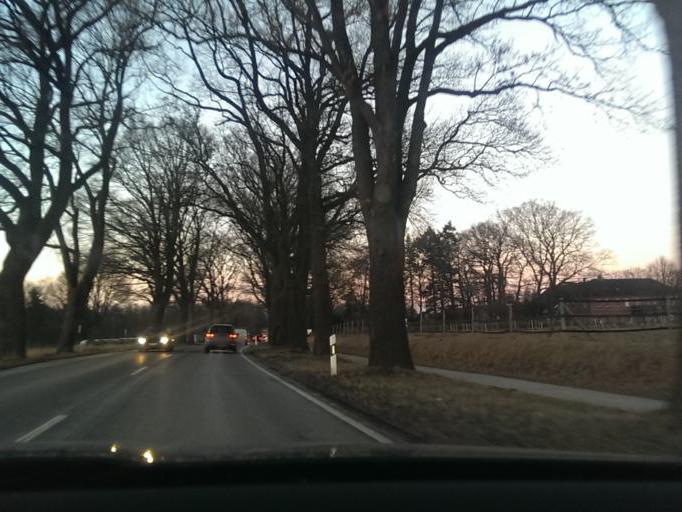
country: DE
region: Lower Saxony
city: Langenhagen
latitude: 52.5051
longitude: 9.7274
